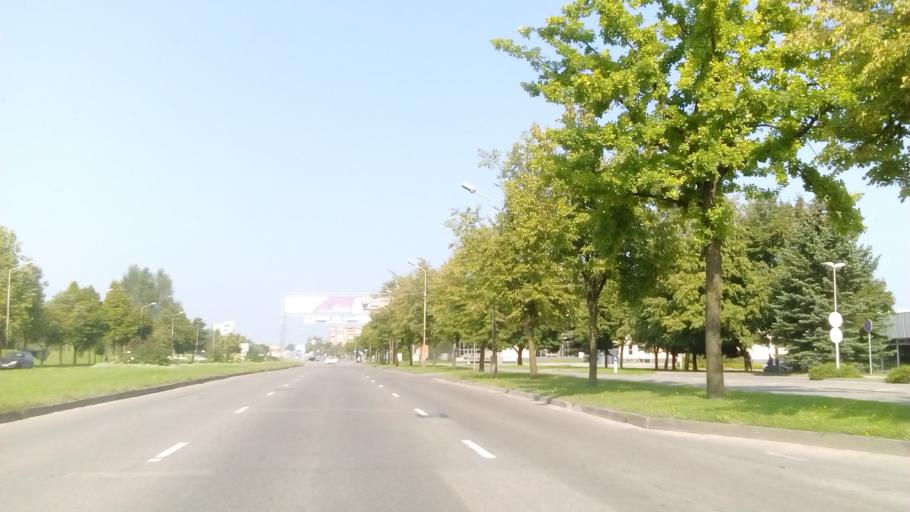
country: LT
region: Alytaus apskritis
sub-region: Alytus
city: Alytus
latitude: 54.4022
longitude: 24.0225
